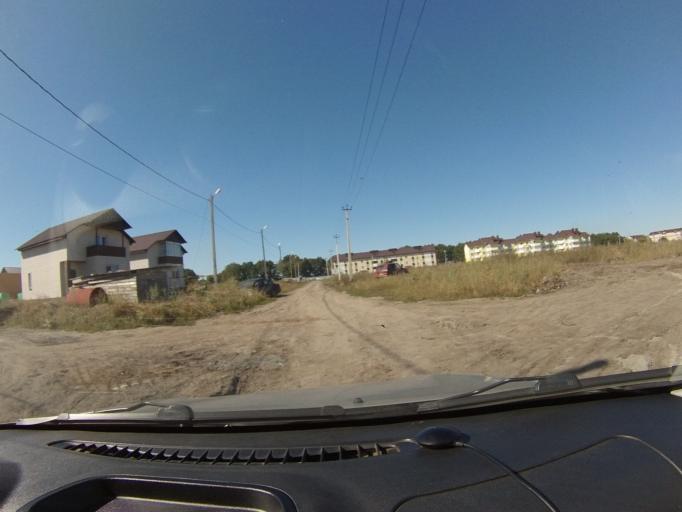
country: RU
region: Tambov
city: Komsomolets
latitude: 52.7823
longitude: 41.3675
